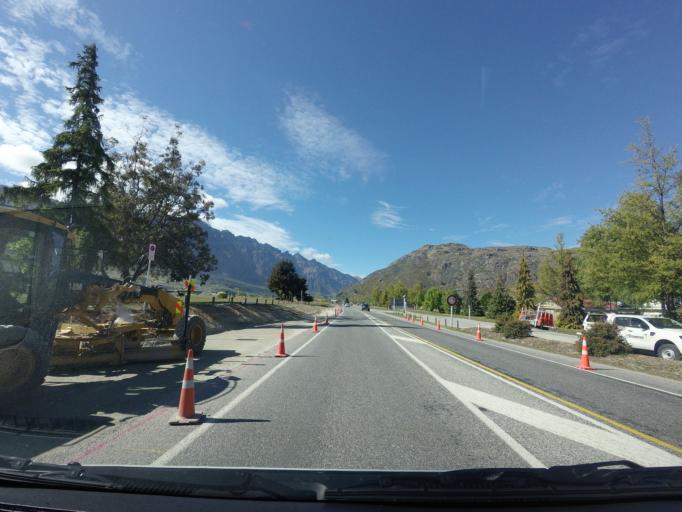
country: NZ
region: Otago
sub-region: Queenstown-Lakes District
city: Queenstown
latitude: -45.0175
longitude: 168.7324
